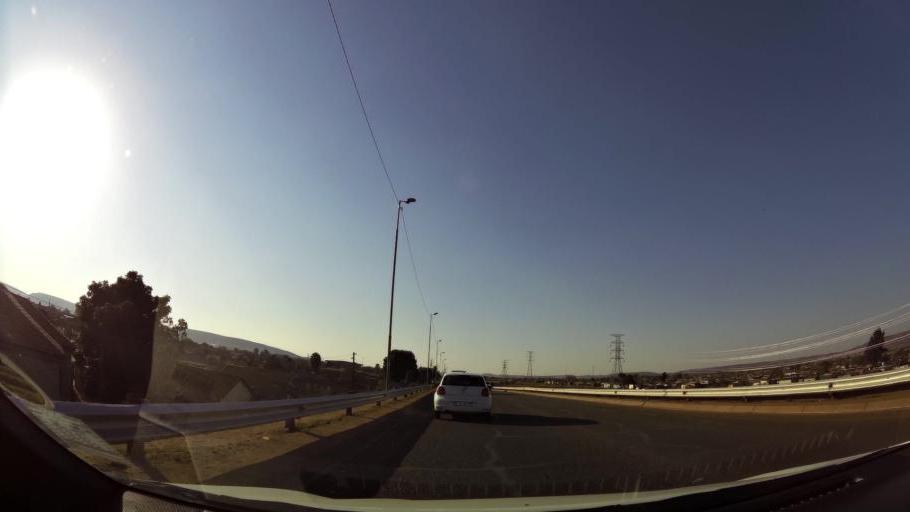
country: ZA
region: Gauteng
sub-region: City of Tshwane Metropolitan Municipality
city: Cullinan
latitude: -25.7286
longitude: 28.4002
